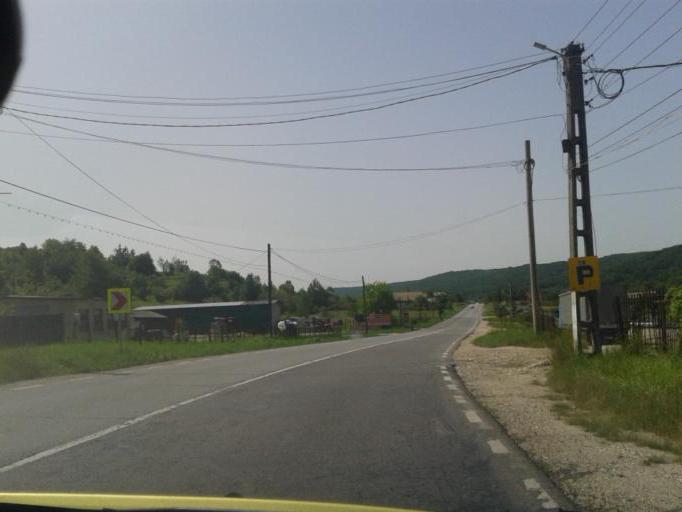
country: RO
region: Arges
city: Draganu-Olteni
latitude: 44.9205
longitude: 24.7211
